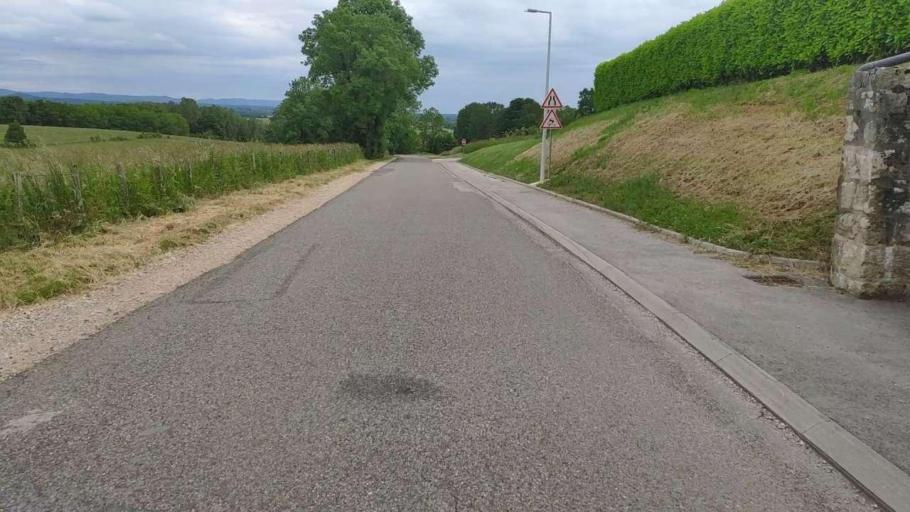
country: FR
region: Franche-Comte
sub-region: Departement du Jura
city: Bletterans
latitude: 46.7813
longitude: 5.5055
